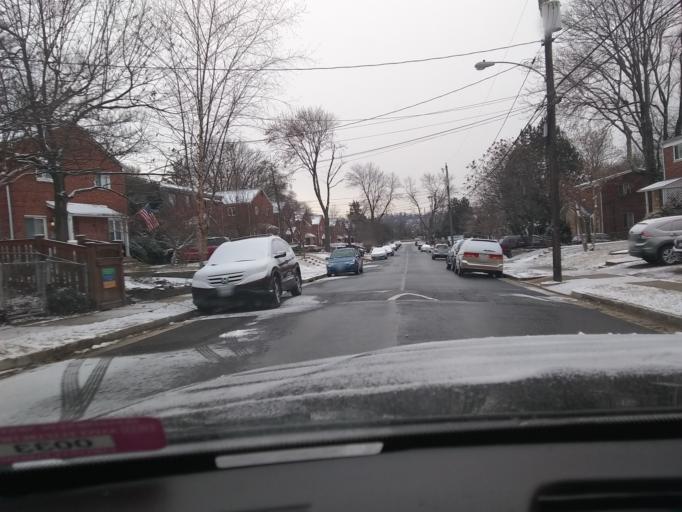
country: US
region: Virginia
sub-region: Fairfax County
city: Huntington
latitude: 38.8088
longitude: -77.0741
